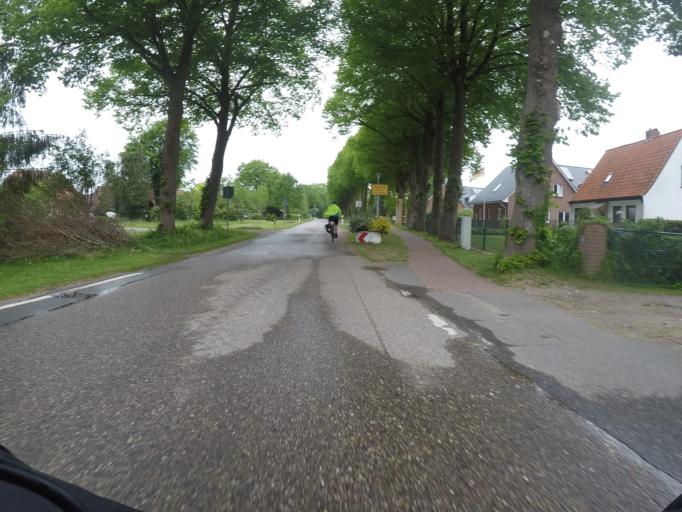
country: DE
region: Schleswig-Holstein
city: Rickling
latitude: 54.0033
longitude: 10.1594
